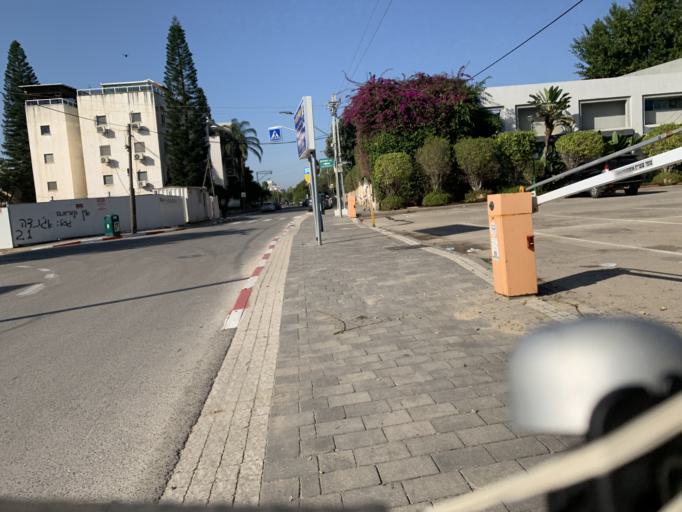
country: IL
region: Tel Aviv
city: Ramat Gan
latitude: 32.0950
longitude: 34.8113
